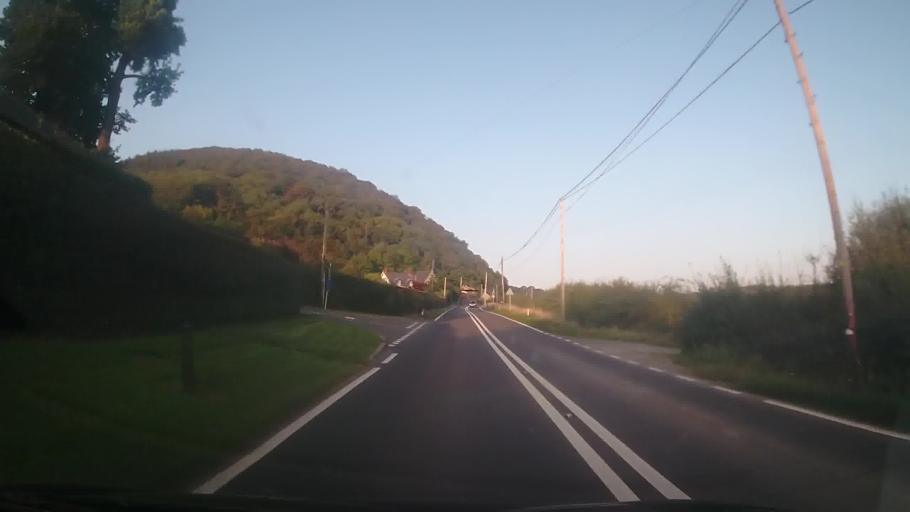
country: GB
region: England
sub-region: Shropshire
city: Pant
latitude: 52.6965
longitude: -3.0643
